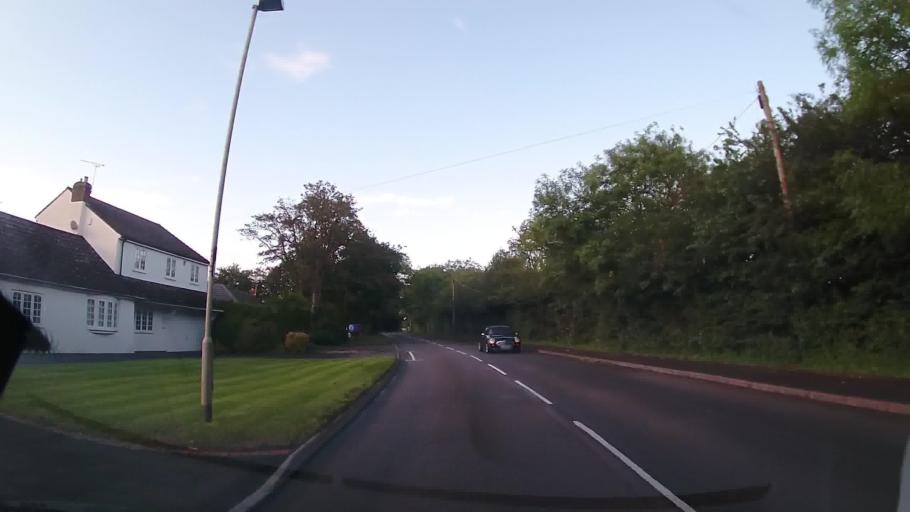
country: GB
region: England
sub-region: Leicestershire
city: Markfield
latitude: 52.6768
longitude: -1.2749
